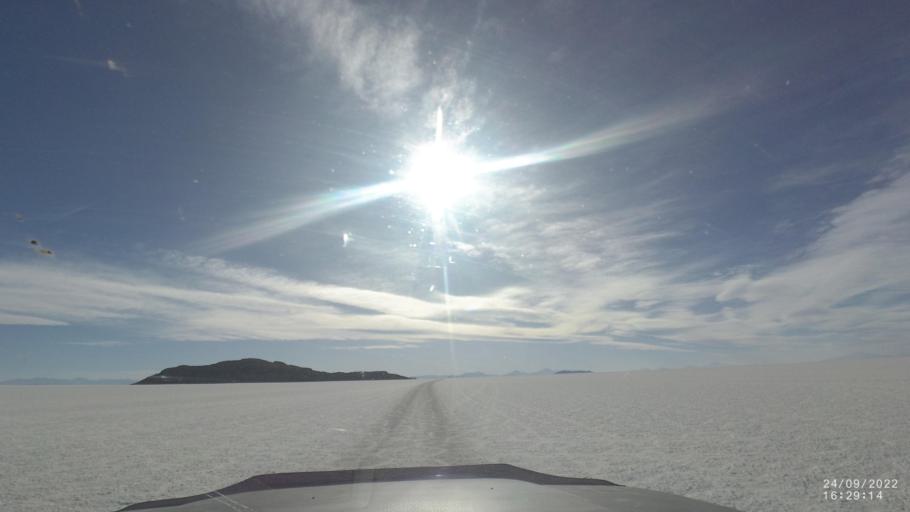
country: BO
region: Potosi
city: Colchani
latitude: -20.2404
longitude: -67.6123
